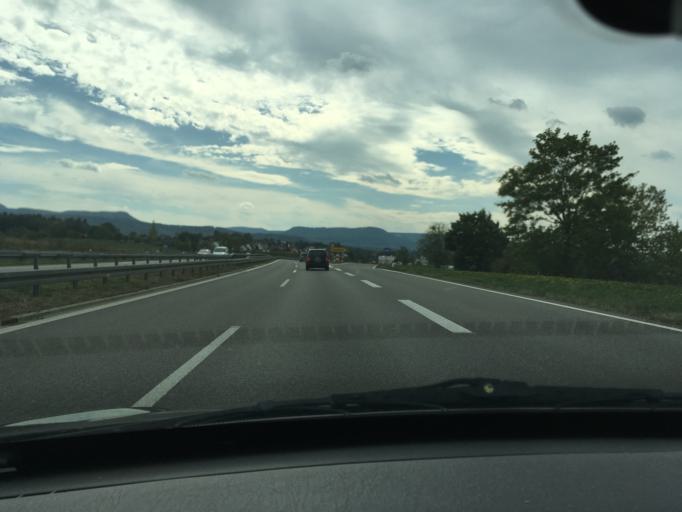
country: DE
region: Baden-Wuerttemberg
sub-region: Tuebingen Region
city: Dusslingen
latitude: 48.4599
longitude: 9.0614
